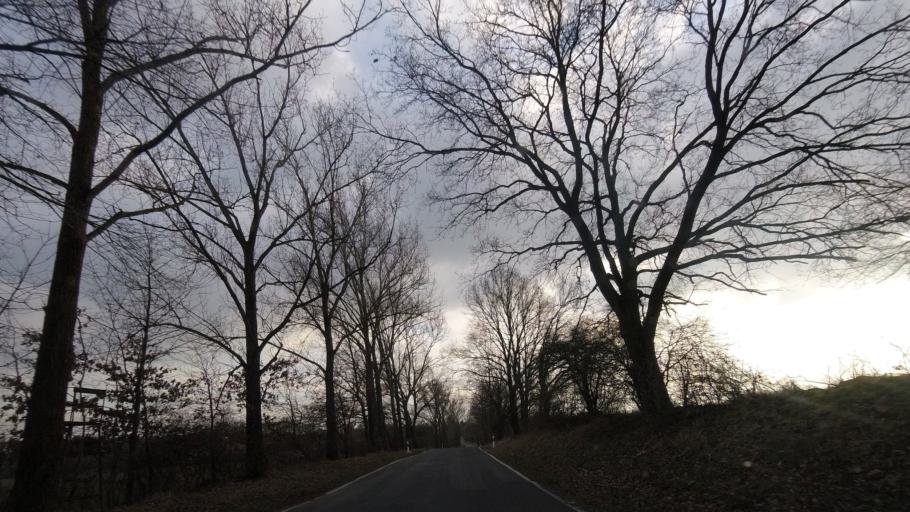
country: DE
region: Brandenburg
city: Wiesenburg
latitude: 52.1444
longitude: 12.5194
